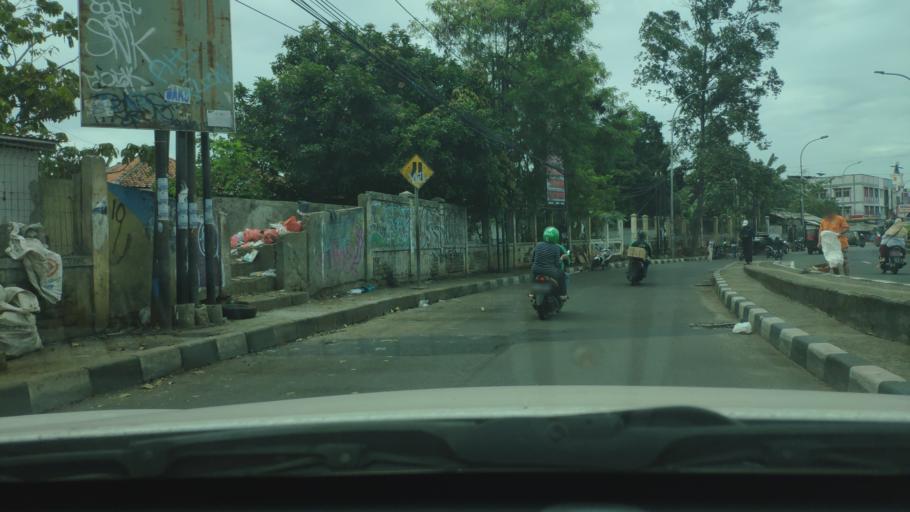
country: ID
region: West Java
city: Ciputat
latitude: -6.2253
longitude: 106.7035
